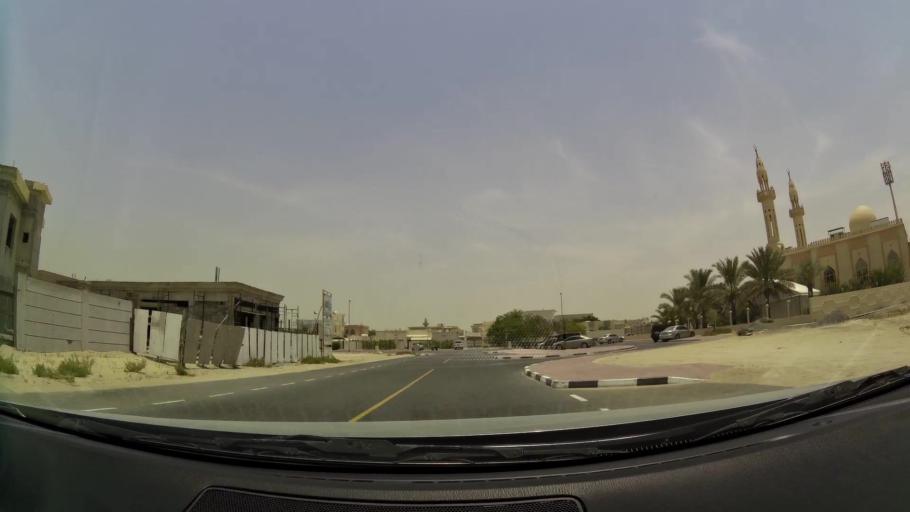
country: AE
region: Ash Shariqah
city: Sharjah
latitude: 25.2072
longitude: 55.3798
